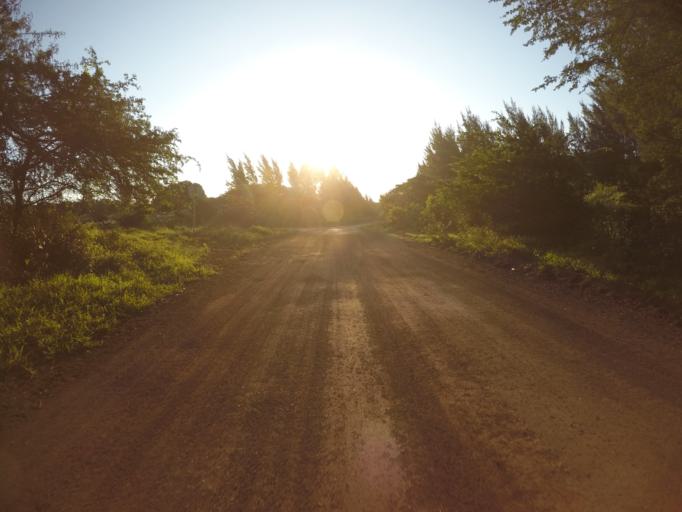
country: ZA
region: KwaZulu-Natal
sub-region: uThungulu District Municipality
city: KwaMbonambi
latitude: -28.6911
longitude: 32.2089
